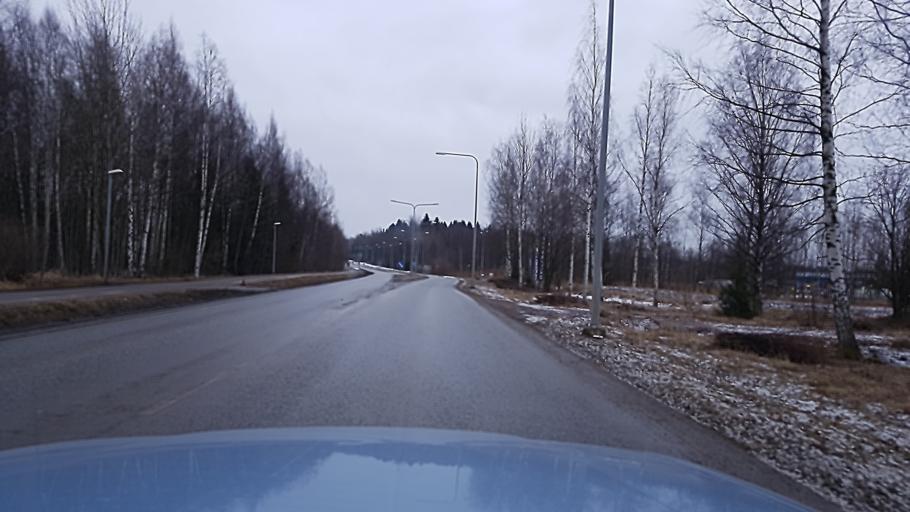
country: FI
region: Uusimaa
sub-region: Helsinki
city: Vantaa
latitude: 60.2642
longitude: 25.0504
